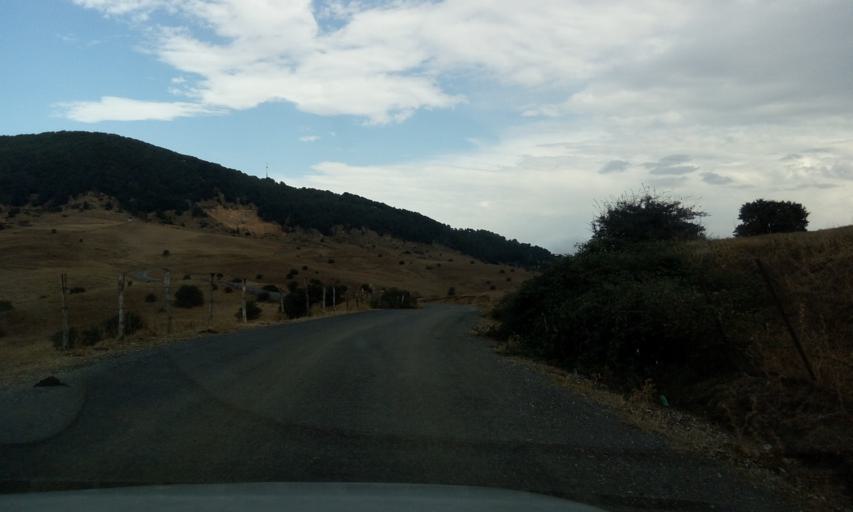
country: DZ
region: Tizi Ouzou
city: Chemini
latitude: 36.6202
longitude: 4.5431
